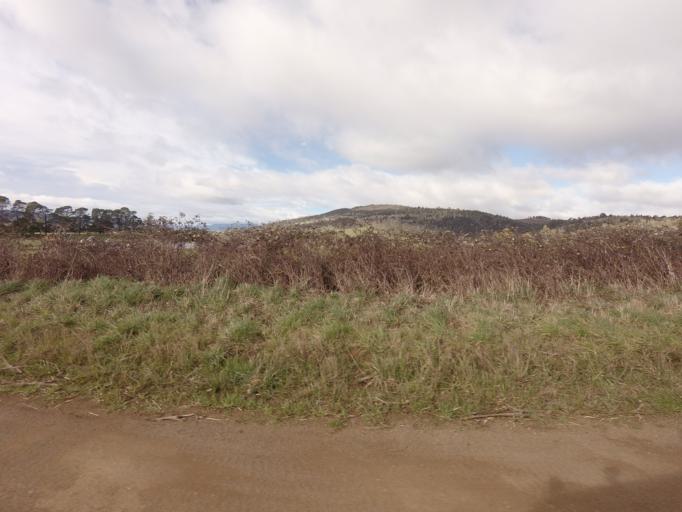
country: AU
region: Tasmania
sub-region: Derwent Valley
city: New Norfolk
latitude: -42.7178
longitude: 146.8759
